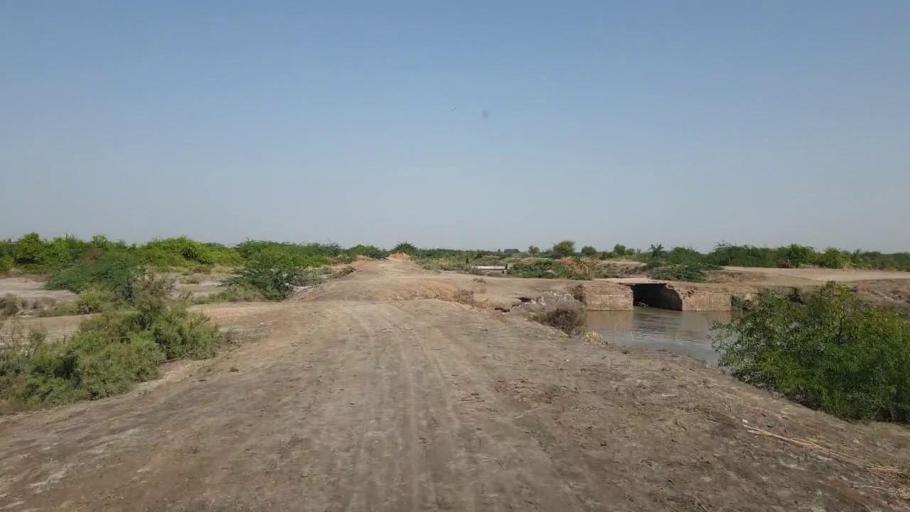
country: PK
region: Sindh
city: Tando Bago
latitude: 24.7082
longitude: 69.0714
